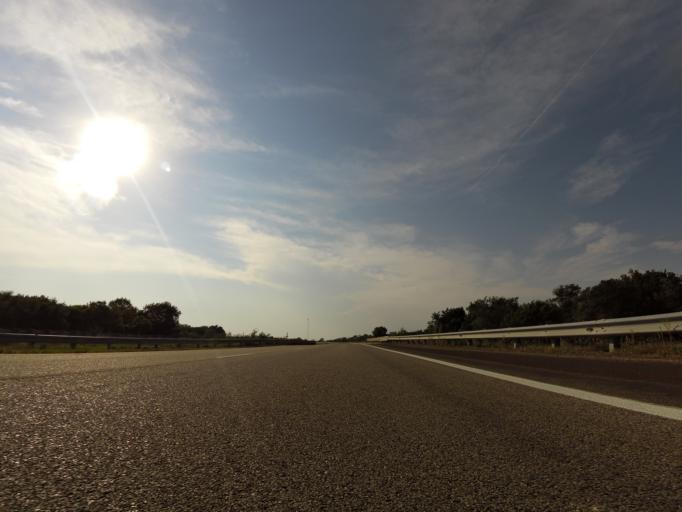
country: US
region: Kansas
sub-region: Reno County
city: South Hutchinson
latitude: 37.9648
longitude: -97.9220
